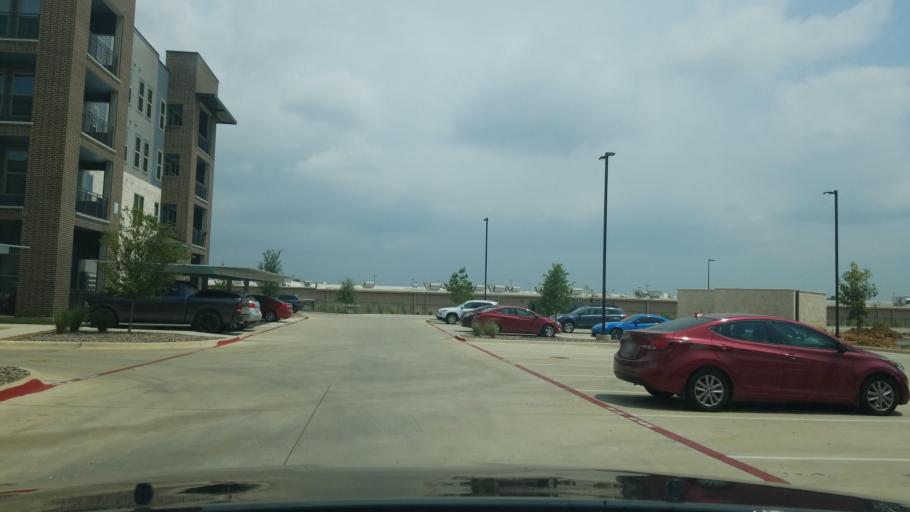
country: US
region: Texas
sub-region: Denton County
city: Corinth
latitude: 33.1895
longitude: -97.0943
